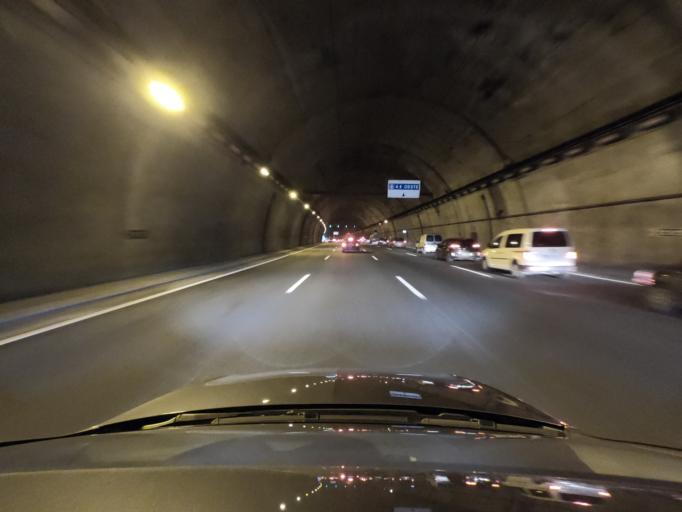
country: PT
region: Lisbon
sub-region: Loures
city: Camarate
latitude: 38.8032
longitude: -9.1412
